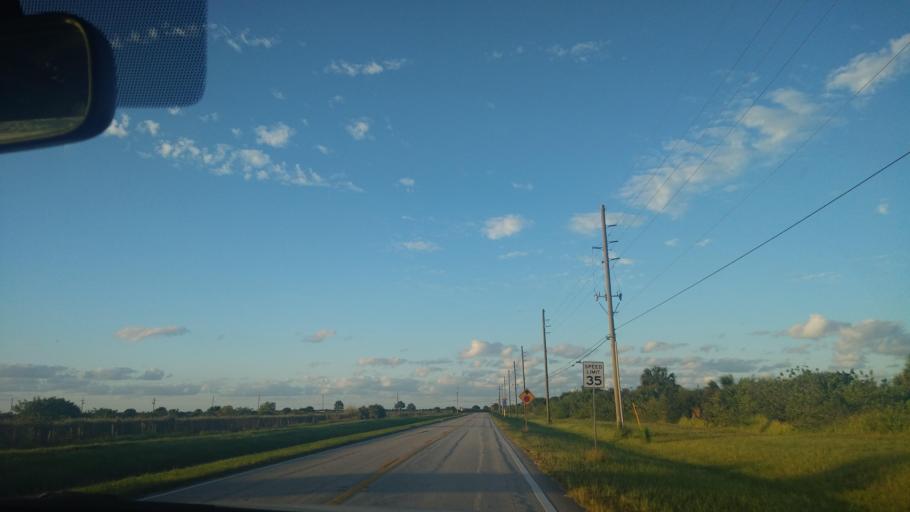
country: US
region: Florida
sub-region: Indian River County
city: Fellsmere
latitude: 27.7361
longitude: -80.6423
